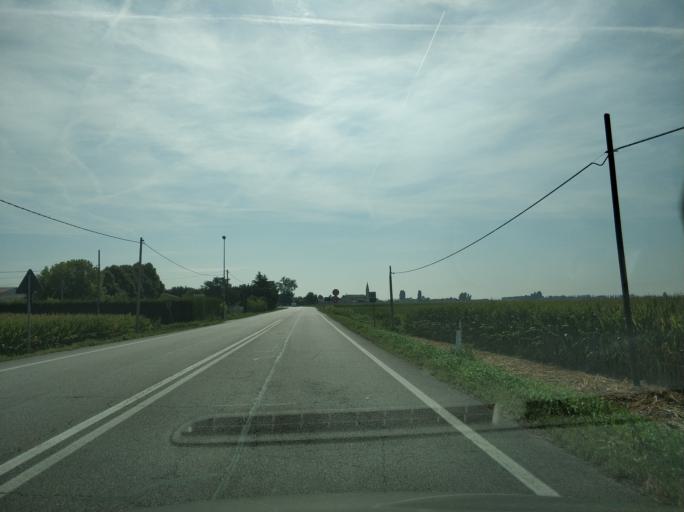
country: IT
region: Veneto
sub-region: Provincia di Padova
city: Correzzola
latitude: 45.2158
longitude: 12.0701
